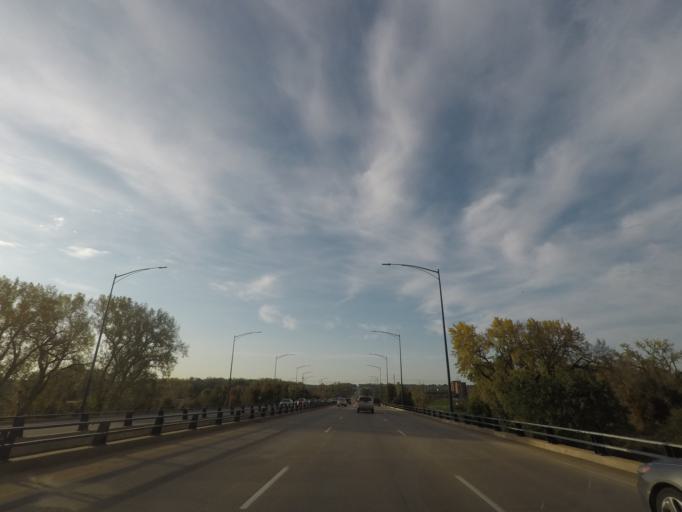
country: US
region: Iowa
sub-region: Polk County
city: Des Moines
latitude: 41.5823
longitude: -93.6449
